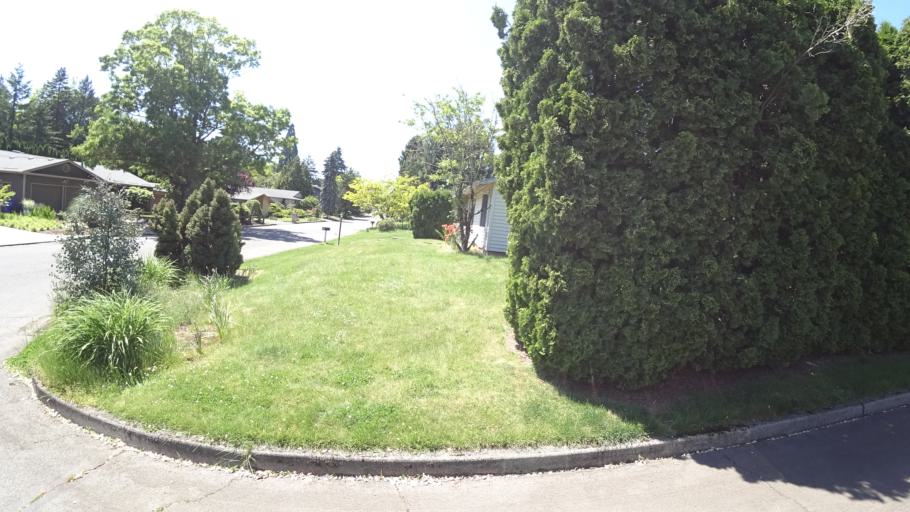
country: US
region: Oregon
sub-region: Washington County
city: Metzger
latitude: 45.4532
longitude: -122.7097
